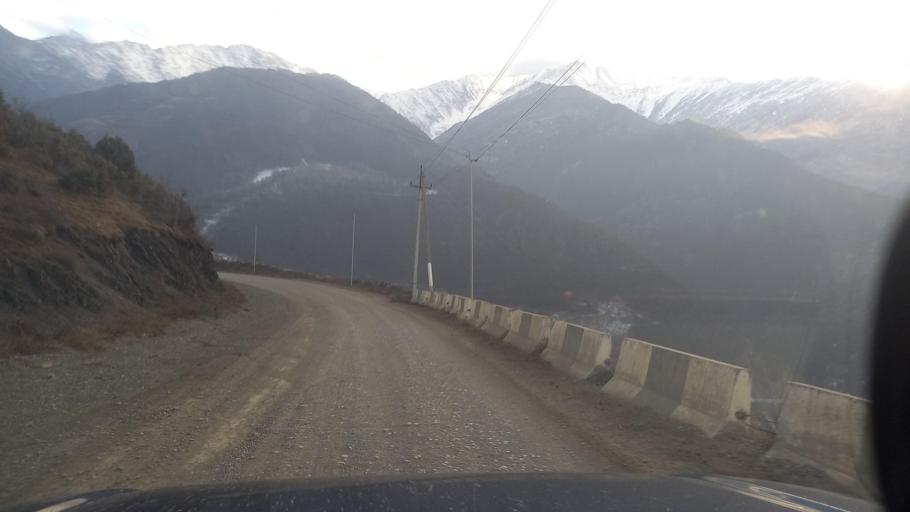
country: RU
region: Ingushetiya
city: Dzhayrakh
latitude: 42.8218
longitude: 44.7044
